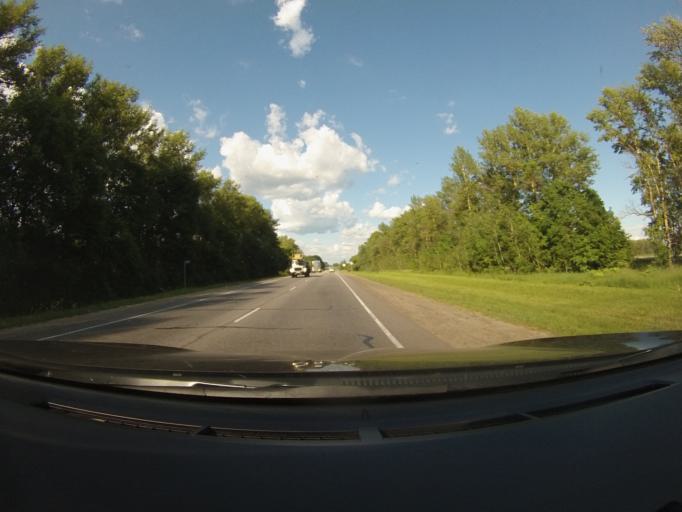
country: RU
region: Tula
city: Bol'shoye Skuratovo
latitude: 53.4379
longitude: 36.8176
